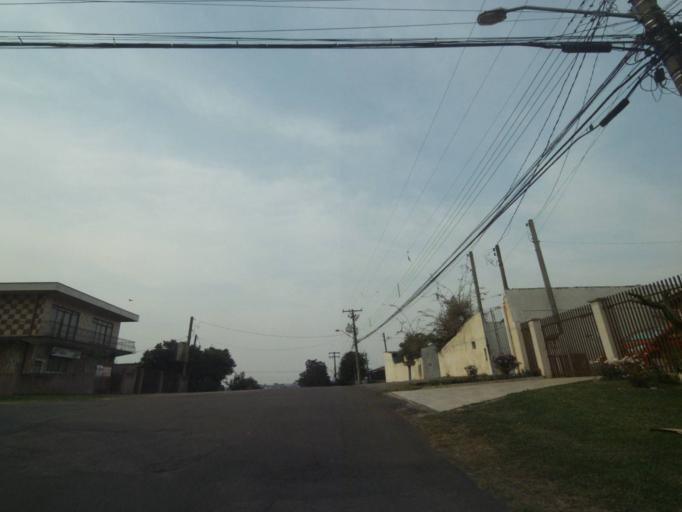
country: BR
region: Parana
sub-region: Sao Jose Dos Pinhais
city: Sao Jose dos Pinhais
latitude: -25.5208
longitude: -49.2749
